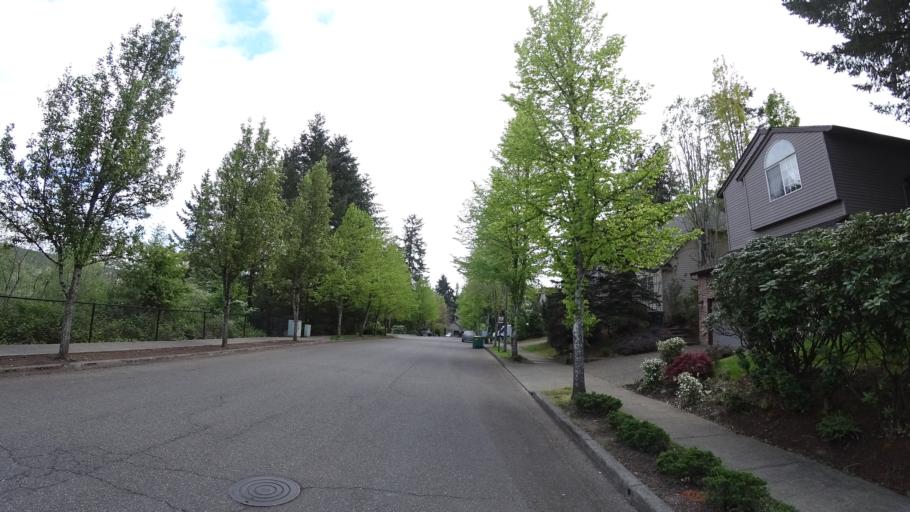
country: US
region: Oregon
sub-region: Washington County
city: Beaverton
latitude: 45.4474
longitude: -122.8296
